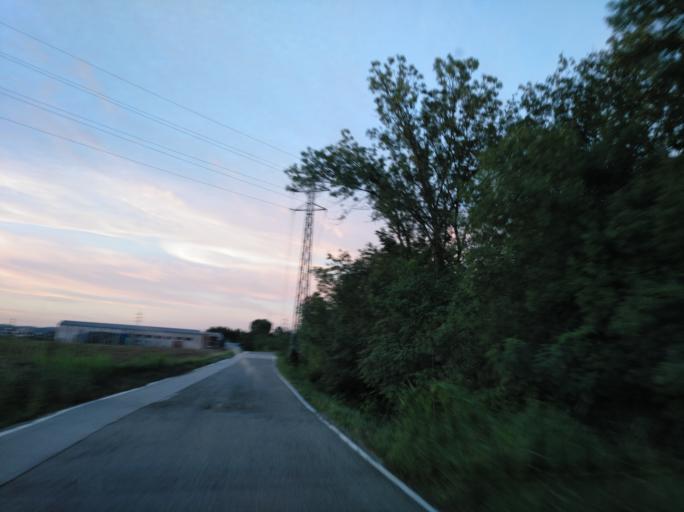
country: ES
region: Catalonia
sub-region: Provincia de Girona
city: Vilablareix
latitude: 41.9553
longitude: 2.7921
